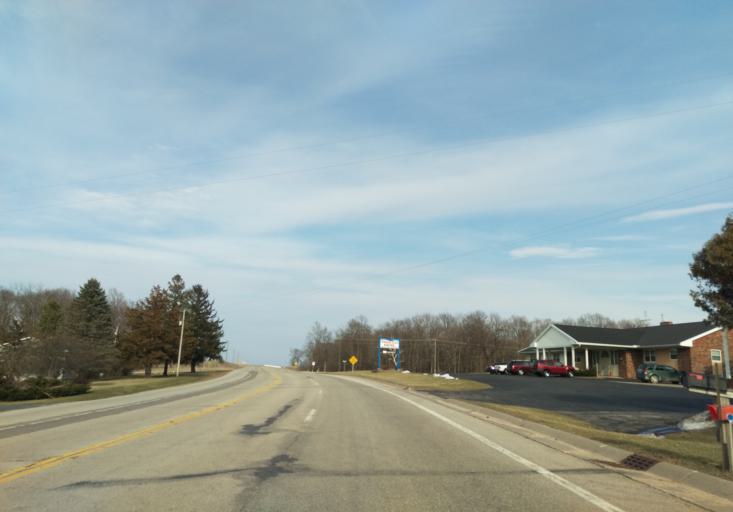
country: US
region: Wisconsin
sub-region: Grant County
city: Fennimore
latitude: 42.9895
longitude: -90.7106
